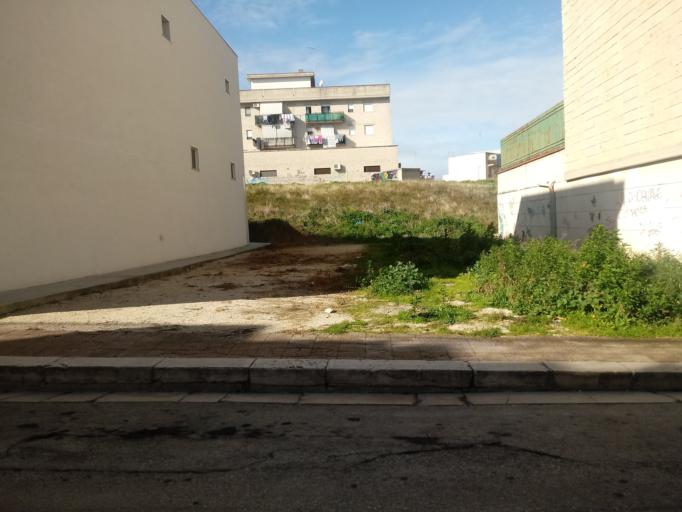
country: IT
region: Apulia
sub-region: Provincia di Barletta - Andria - Trani
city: Andria
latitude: 41.2193
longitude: 16.2946
